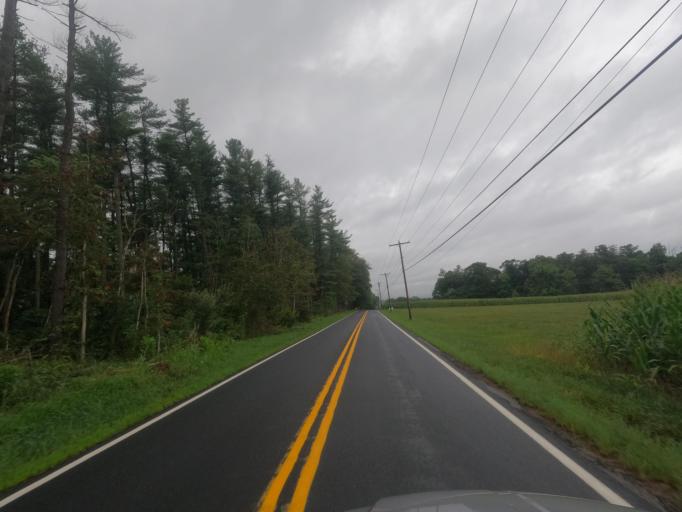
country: US
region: West Virginia
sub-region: Berkeley County
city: Martinsburg
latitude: 39.6177
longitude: -77.9991
